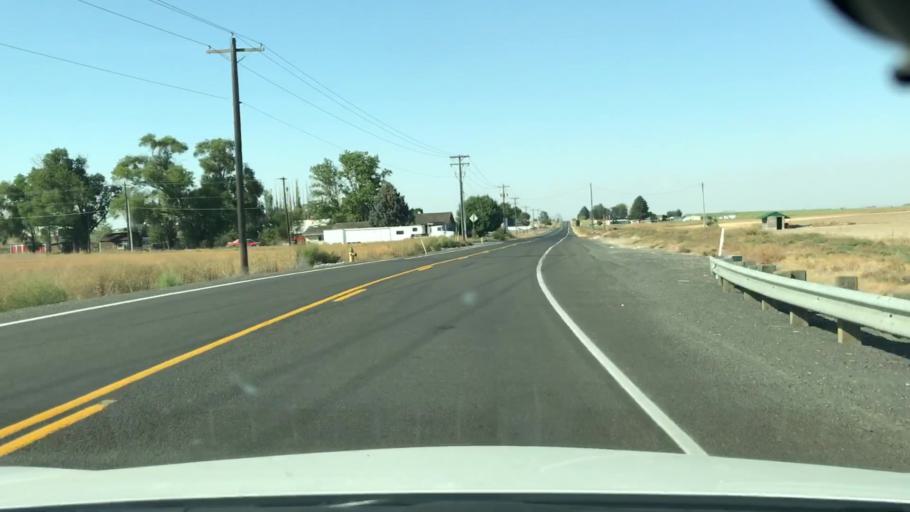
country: US
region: Washington
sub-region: Grant County
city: Moses Lake
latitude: 47.1003
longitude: -119.2362
